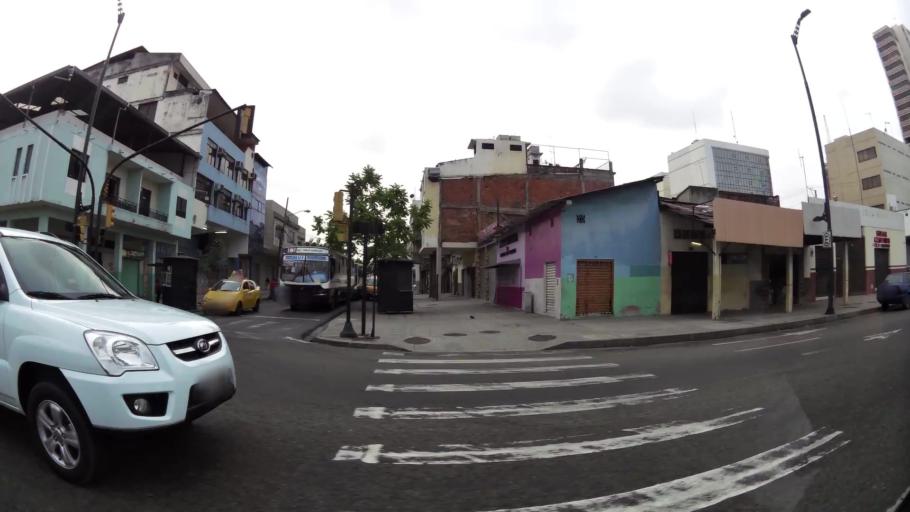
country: EC
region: Guayas
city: Guayaquil
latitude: -2.1875
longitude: -79.8894
